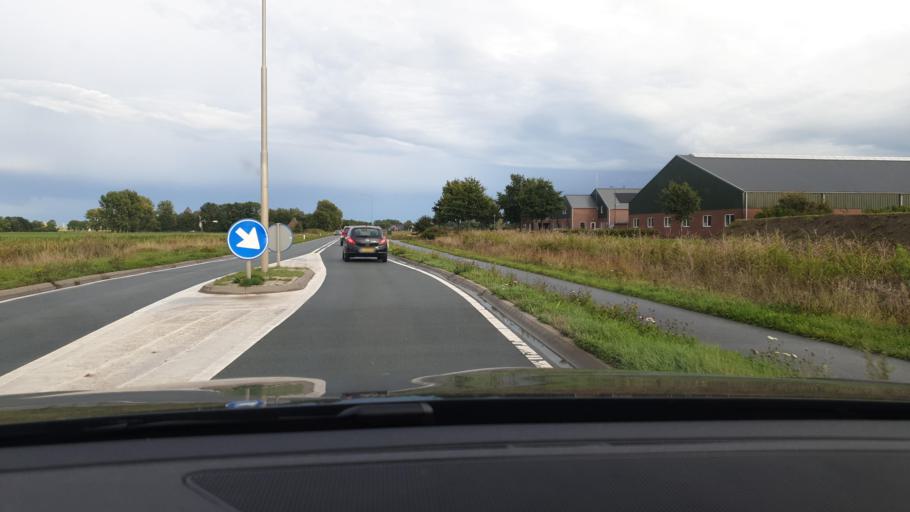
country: NL
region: North Brabant
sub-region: Gemeente Oss
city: Berghem
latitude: 51.8024
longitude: 5.6076
